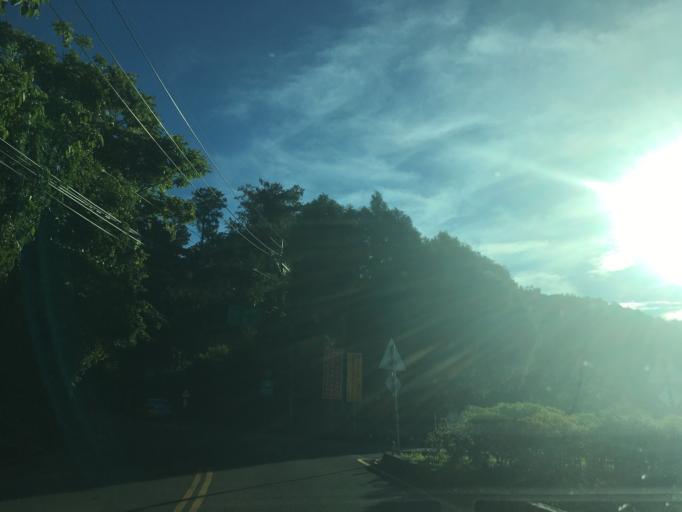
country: TW
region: Taiwan
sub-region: Nantou
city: Puli
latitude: 24.0238
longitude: 121.1344
